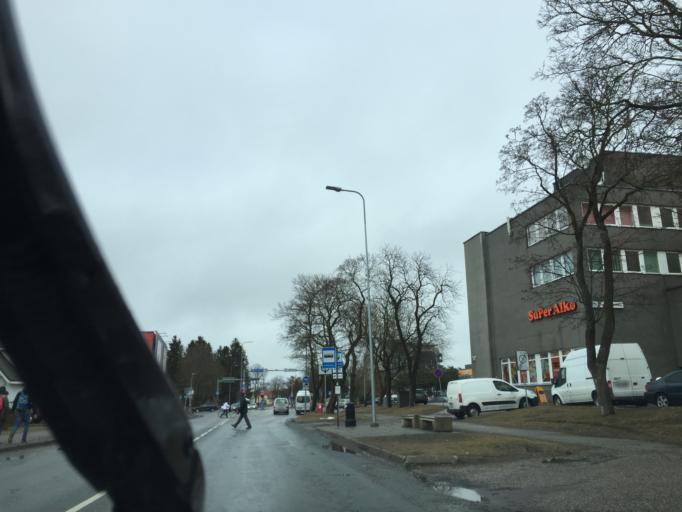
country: EE
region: Laeaene
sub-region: Haapsalu linn
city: Haapsalu
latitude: 58.9382
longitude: 23.5415
